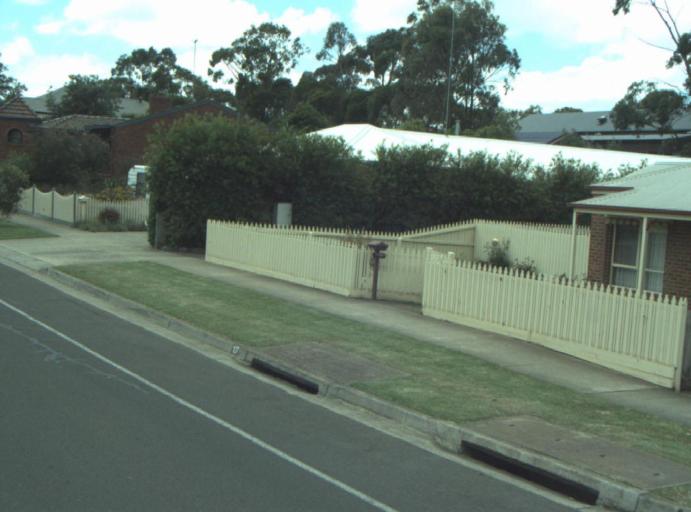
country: AU
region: Victoria
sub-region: Greater Geelong
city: Wandana Heights
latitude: -38.1946
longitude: 144.3171
